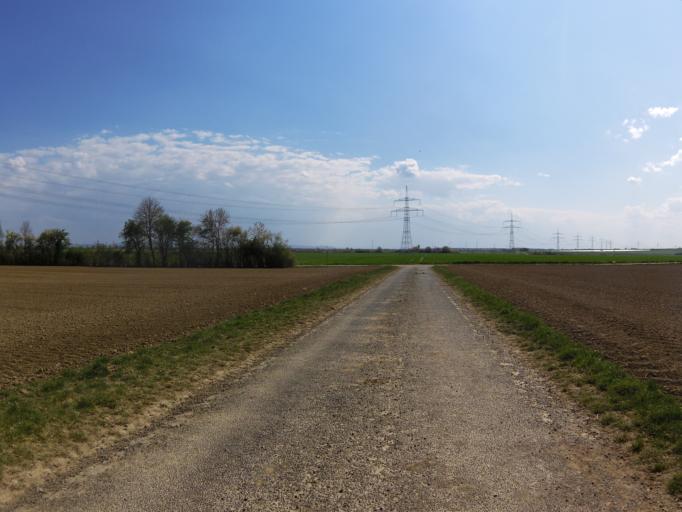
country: DE
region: Bavaria
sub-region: Regierungsbezirk Unterfranken
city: Oberpleichfeld
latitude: 49.8430
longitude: 10.0897
